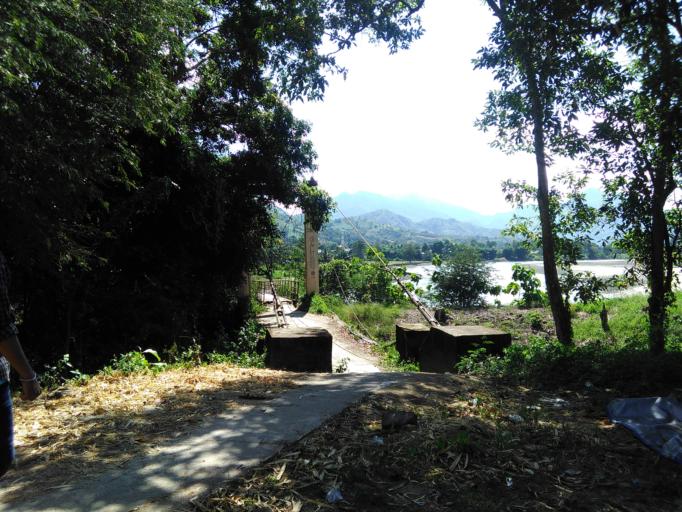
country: ID
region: South Sulawesi
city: Enrekang
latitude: -3.5194
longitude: 119.7330
